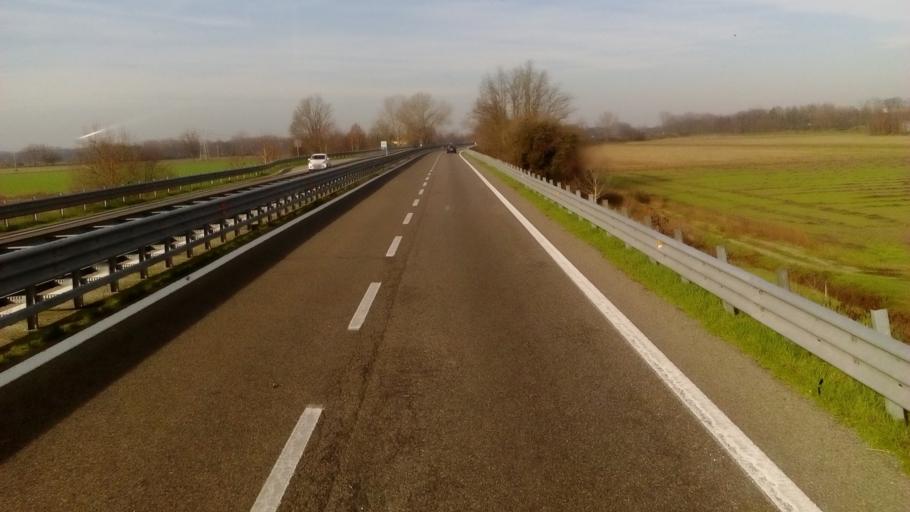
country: IT
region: Lombardy
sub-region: Provincia di Lodi
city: Fombio
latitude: 45.1329
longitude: 9.6799
